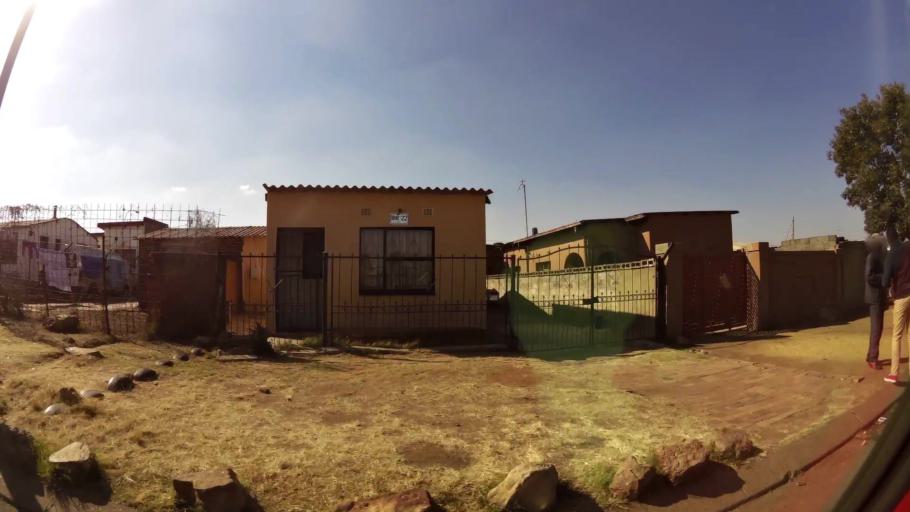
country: ZA
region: Gauteng
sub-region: City of Johannesburg Metropolitan Municipality
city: Soweto
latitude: -26.2347
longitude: 27.8820
